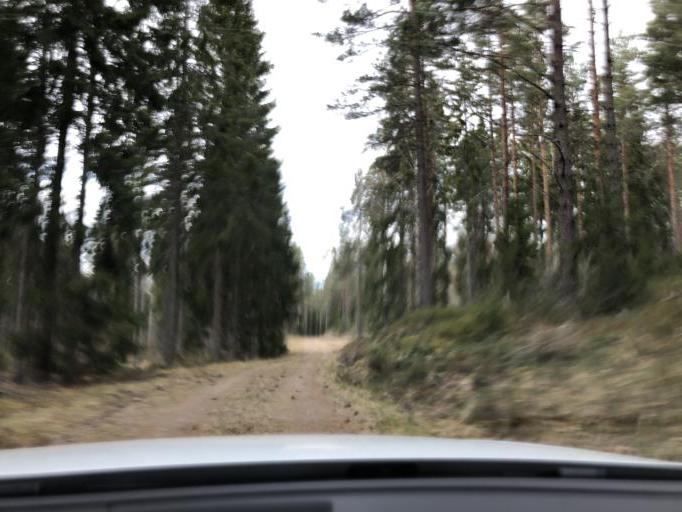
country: SE
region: Gaevleborg
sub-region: Gavle Kommun
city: Hedesunda
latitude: 60.3422
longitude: 17.0660
